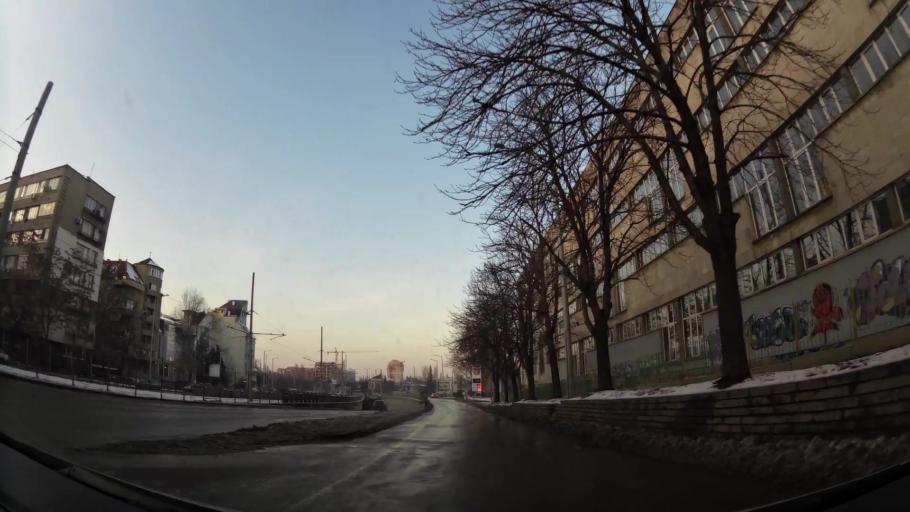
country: BG
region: Sofia-Capital
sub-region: Stolichna Obshtina
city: Sofia
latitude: 42.6951
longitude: 23.3554
